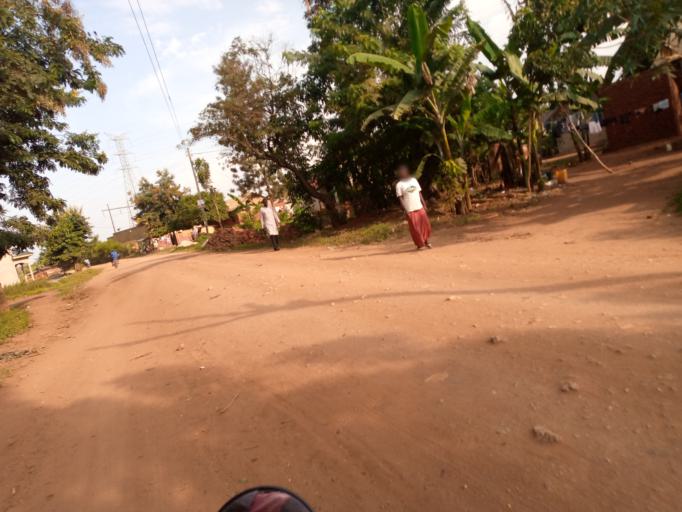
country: UG
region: Eastern Region
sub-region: Mbale District
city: Mbale
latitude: 1.0597
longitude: 34.1555
